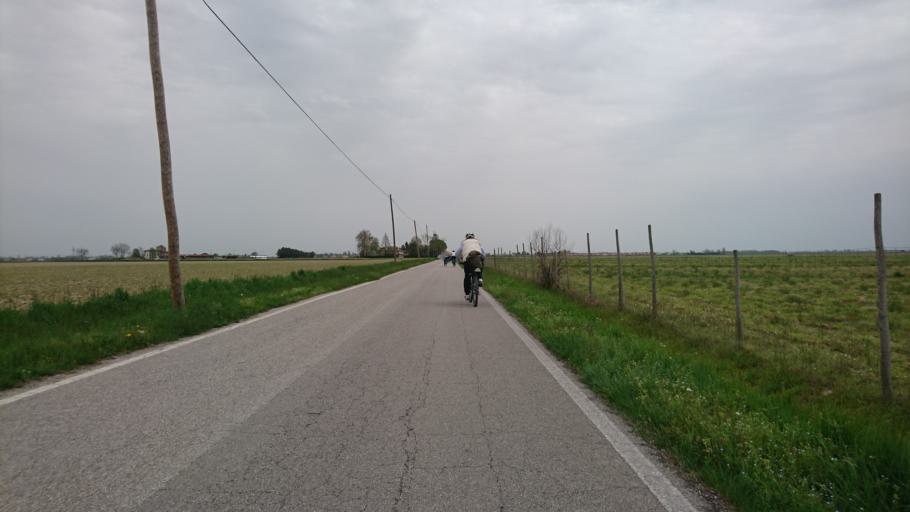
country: IT
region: Veneto
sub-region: Provincia di Venezia
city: Lugugnana
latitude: 45.6994
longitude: 12.9271
